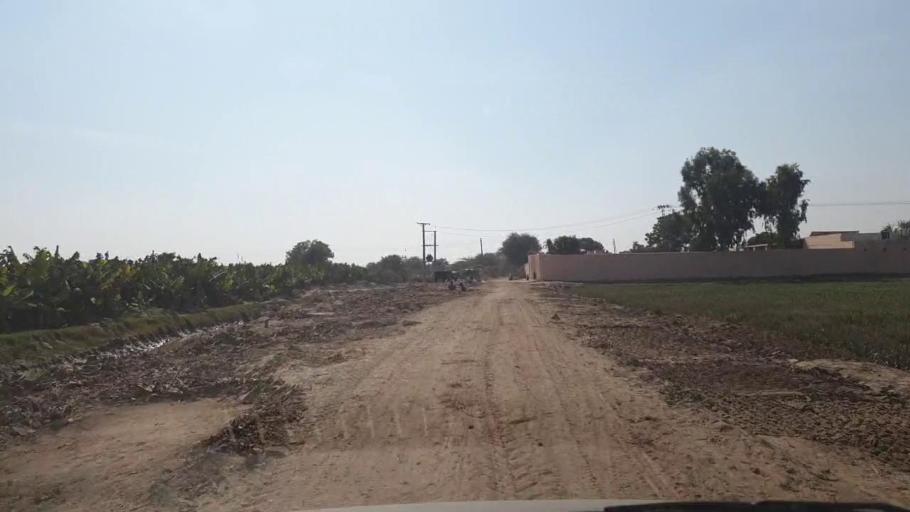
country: PK
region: Sindh
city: Chambar
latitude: 25.3706
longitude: 68.8078
